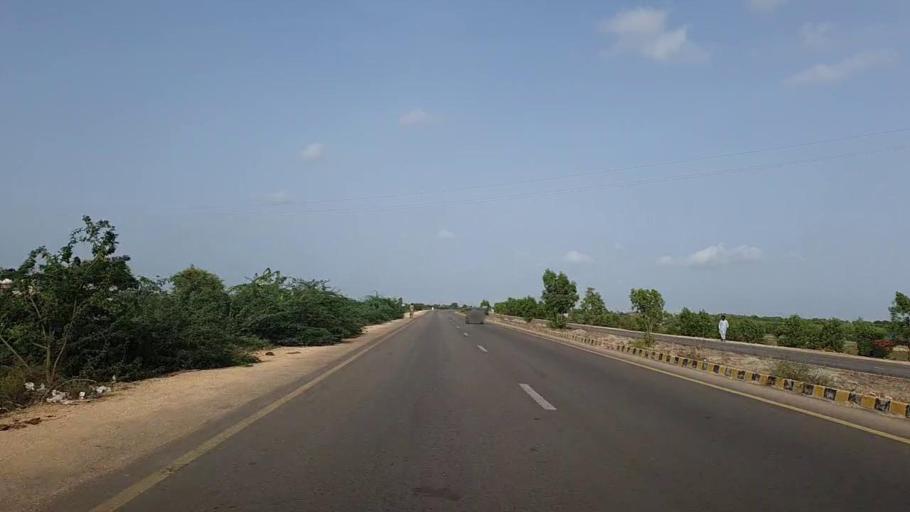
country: PK
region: Sindh
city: Thatta
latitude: 24.7431
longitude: 67.7831
